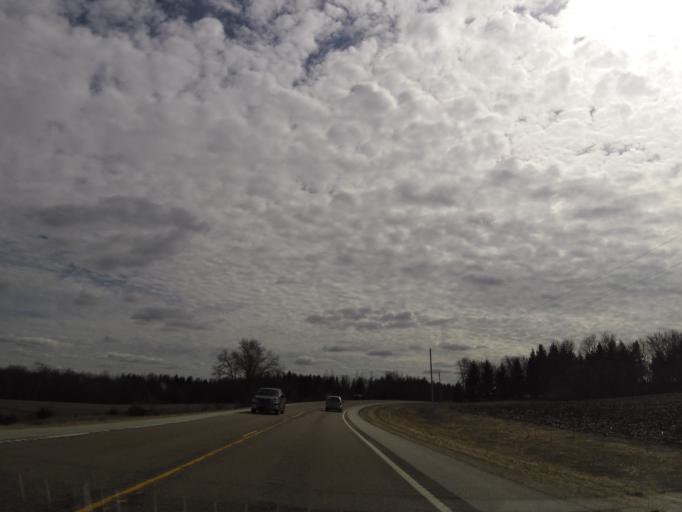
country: US
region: Minnesota
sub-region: Olmsted County
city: Stewartville
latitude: 43.9009
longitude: -92.4085
